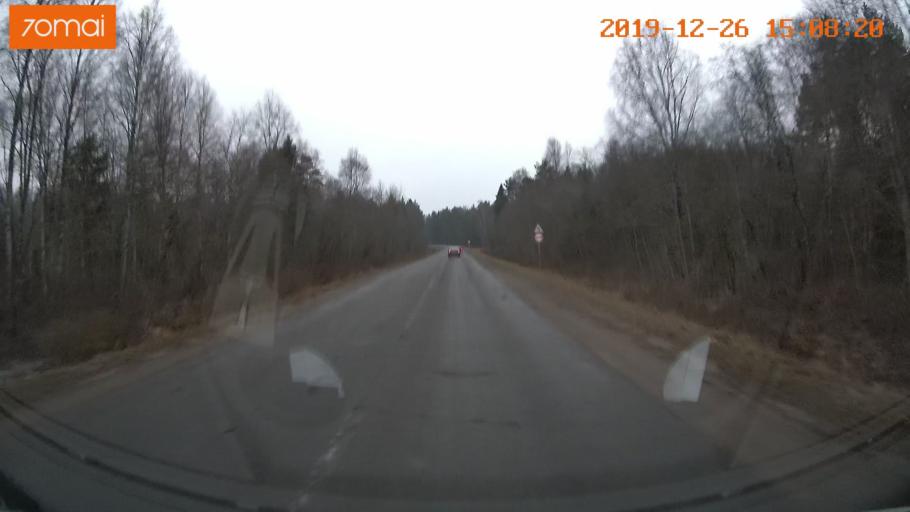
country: RU
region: Jaroslavl
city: Rybinsk
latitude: 58.1609
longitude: 38.8388
